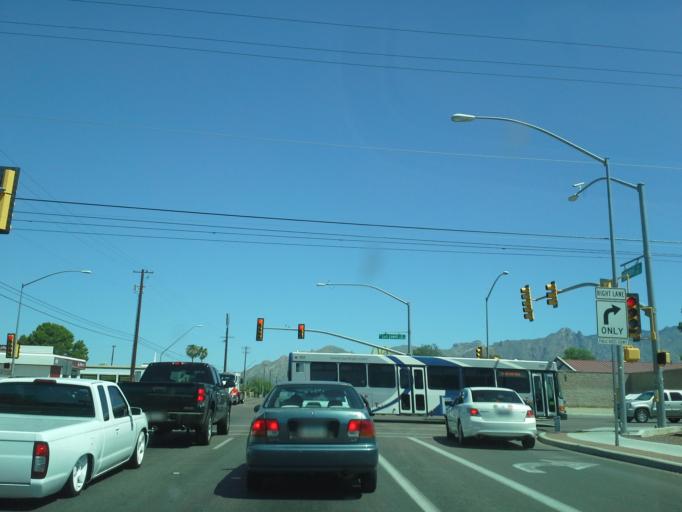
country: US
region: Arizona
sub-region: Pima County
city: Catalina Foothills
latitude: 32.2644
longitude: -110.9437
